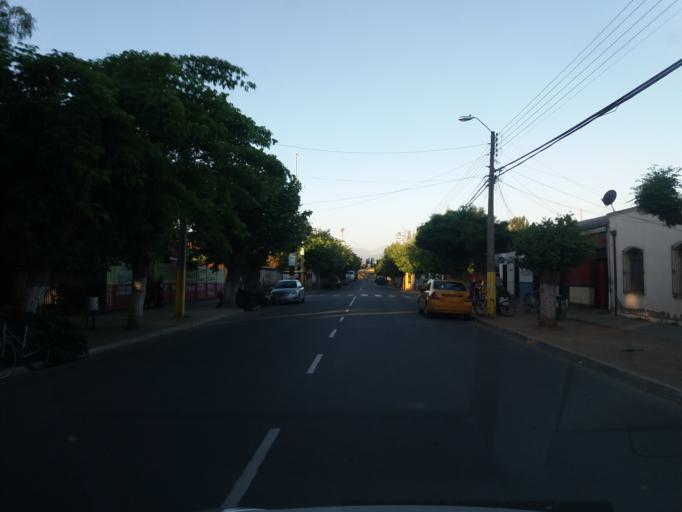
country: CL
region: Valparaiso
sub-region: Provincia de Quillota
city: Quillota
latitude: -32.9381
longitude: -71.2761
